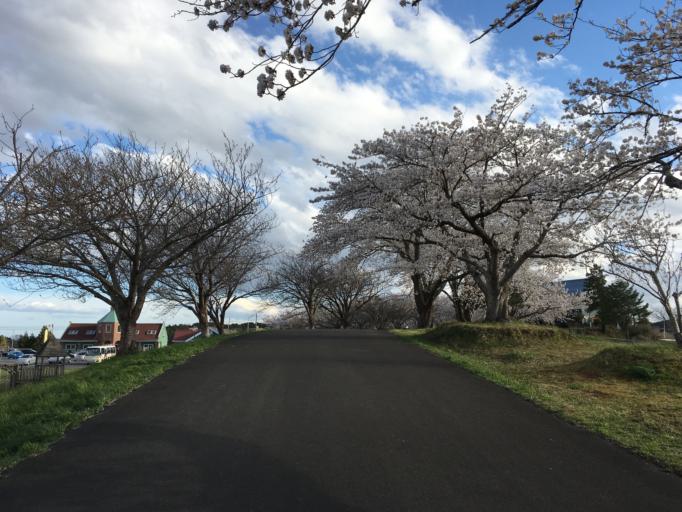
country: JP
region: Miyagi
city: Wakuya
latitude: 38.6900
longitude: 141.1341
